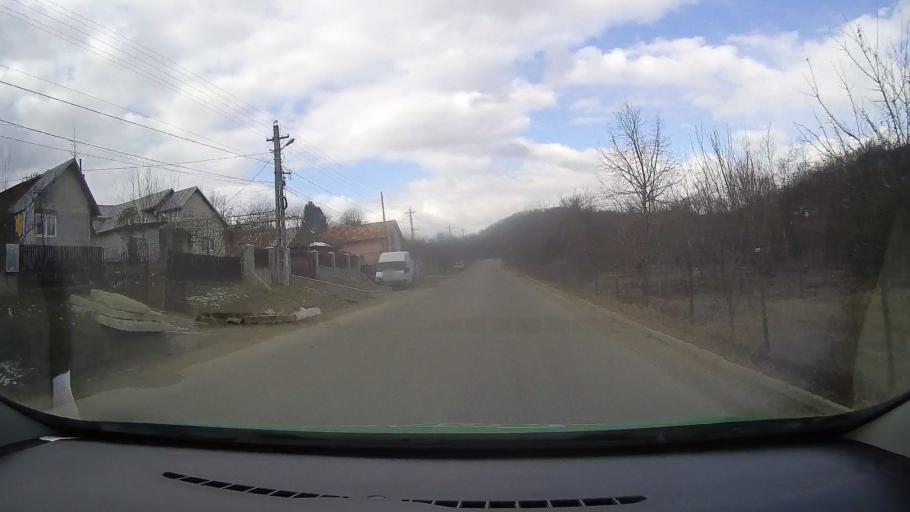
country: RO
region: Dambovita
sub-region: Comuna Valea Lunga
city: Valea Lunga-Cricov
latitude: 45.0653
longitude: 25.5550
